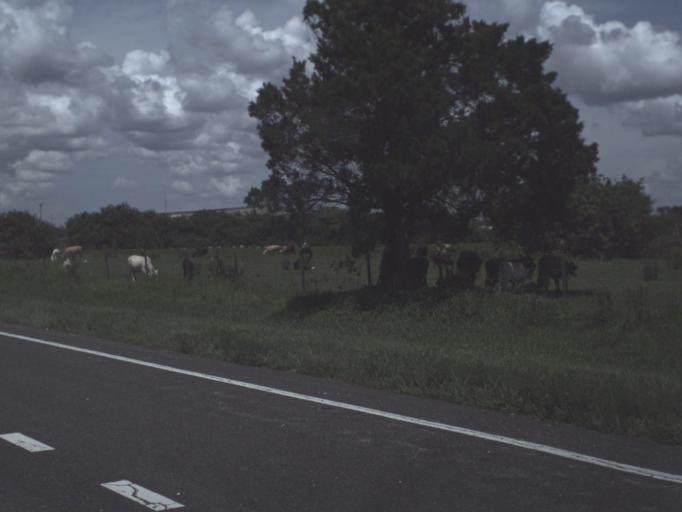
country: US
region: Florida
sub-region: Hillsborough County
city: Apollo Beach
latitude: 27.7947
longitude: -82.3842
